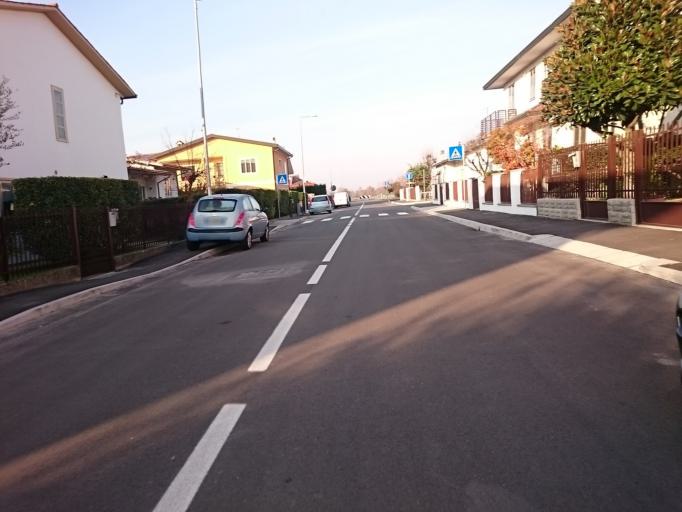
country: IT
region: Veneto
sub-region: Provincia di Padova
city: Ponte San Nicolo
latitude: 45.3674
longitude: 11.9188
